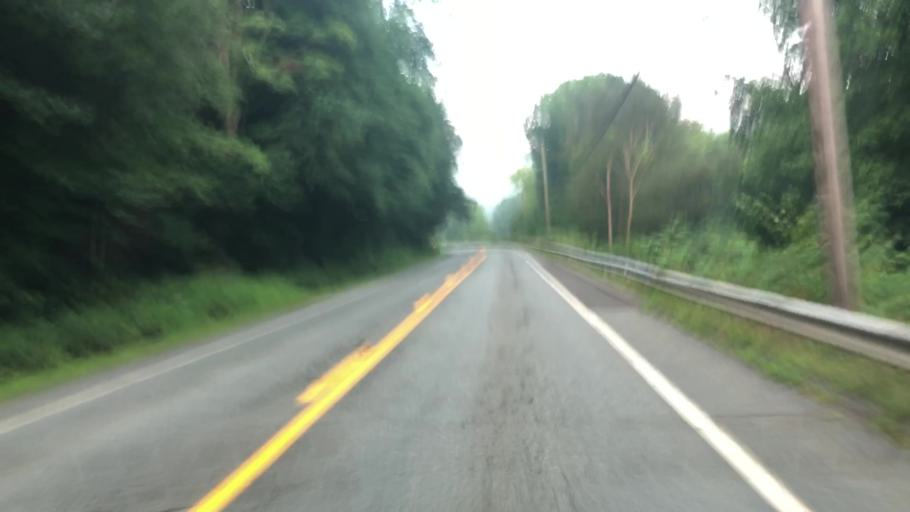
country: US
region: Massachusetts
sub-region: Franklin County
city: Buckland
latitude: 42.5851
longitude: -72.7941
